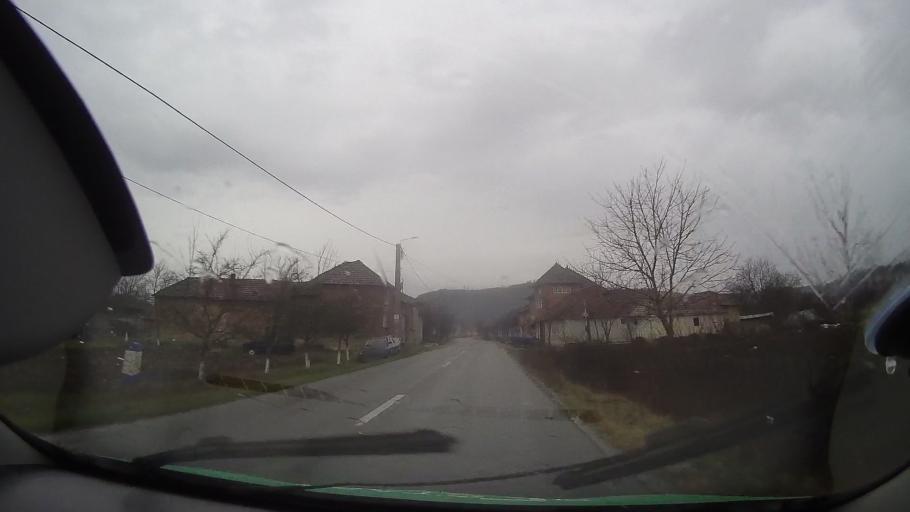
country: RO
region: Bihor
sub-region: Comuna Pocola
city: Pocola
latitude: 46.6901
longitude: 22.2699
